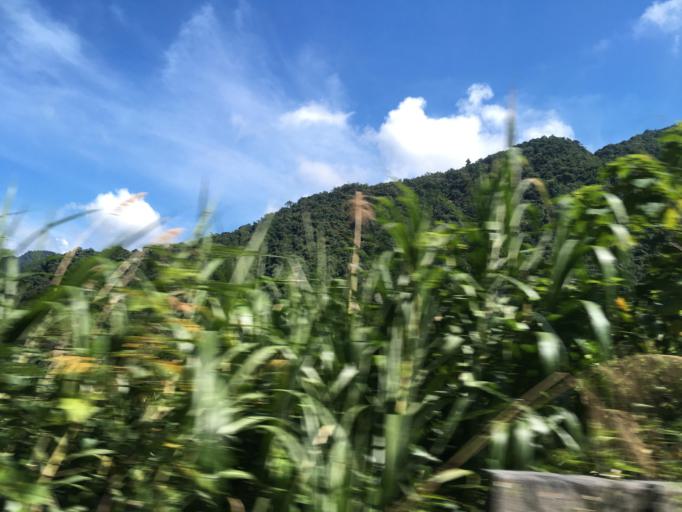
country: TW
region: Taiwan
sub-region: Yilan
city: Yilan
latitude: 24.4198
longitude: 121.7299
